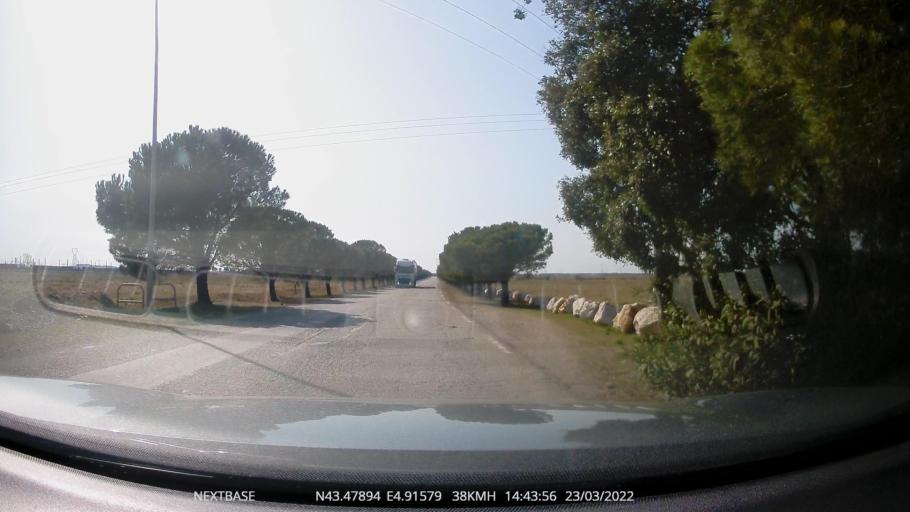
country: FR
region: Provence-Alpes-Cote d'Azur
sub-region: Departement des Bouches-du-Rhone
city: Fos-sur-Mer
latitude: 43.4792
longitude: 4.9180
